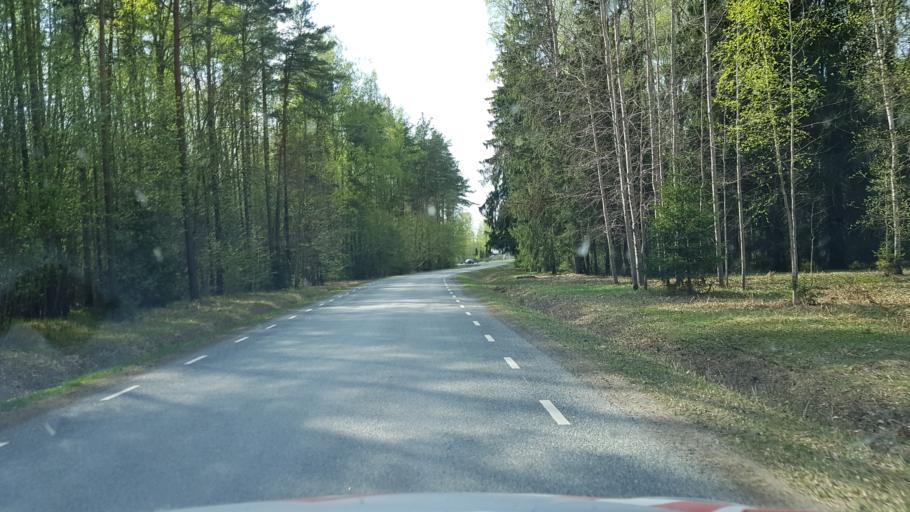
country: EE
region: Paernumaa
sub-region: Paikuse vald
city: Paikuse
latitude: 58.4444
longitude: 24.5879
